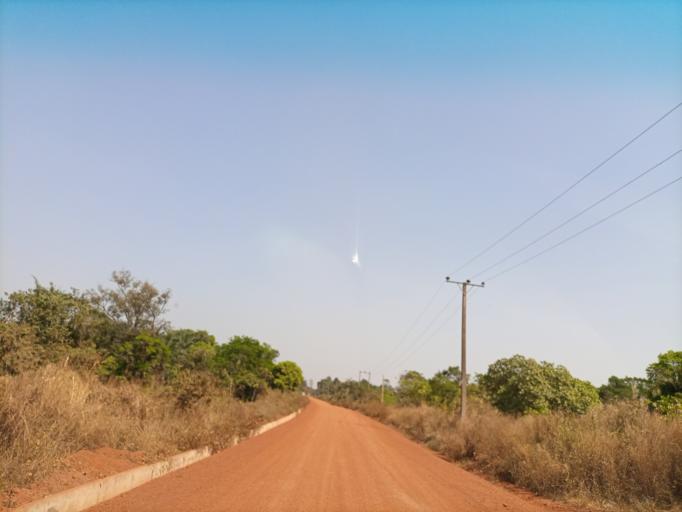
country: NG
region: Enugu
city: Nsukka
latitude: 6.7993
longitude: 7.3465
